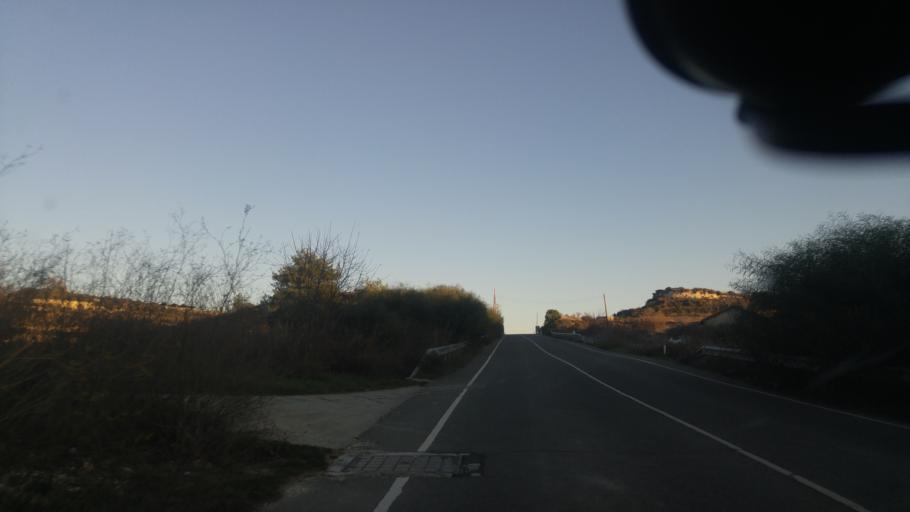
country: CY
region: Limassol
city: Pachna
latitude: 34.7986
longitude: 32.7993
